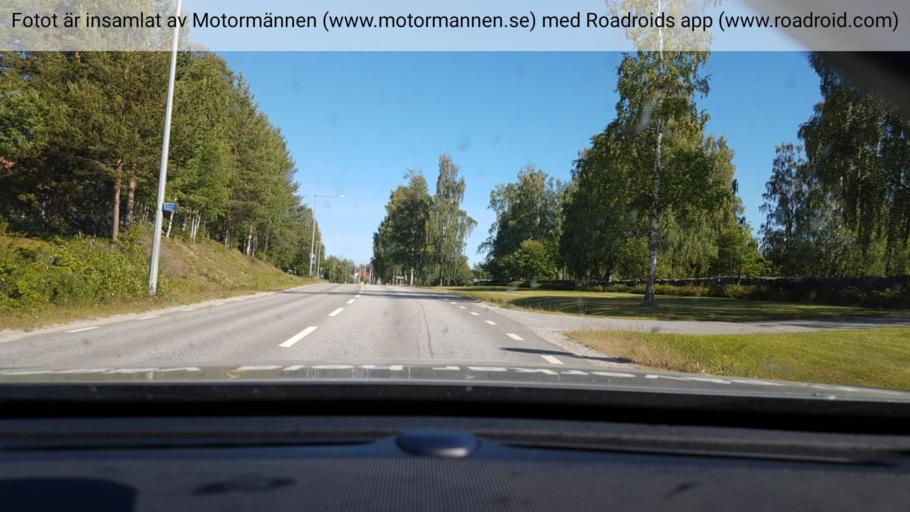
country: SE
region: Vaesterbotten
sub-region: Lycksele Kommun
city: Lycksele
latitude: 64.6081
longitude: 18.6495
